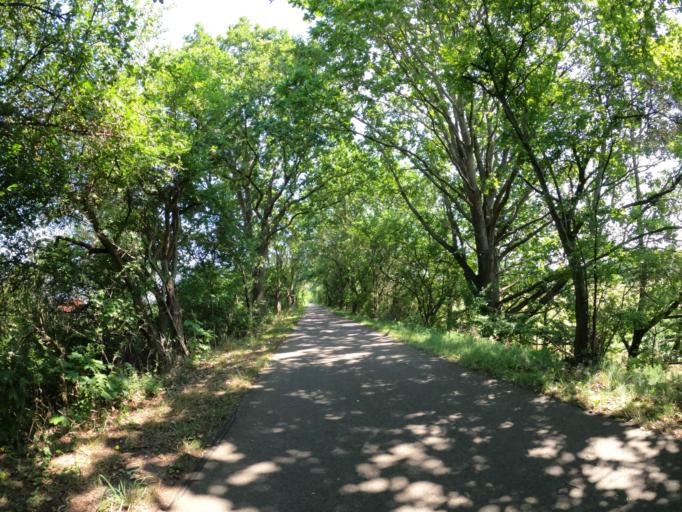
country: DE
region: Brandenburg
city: Templin
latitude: 53.2557
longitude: 13.5295
